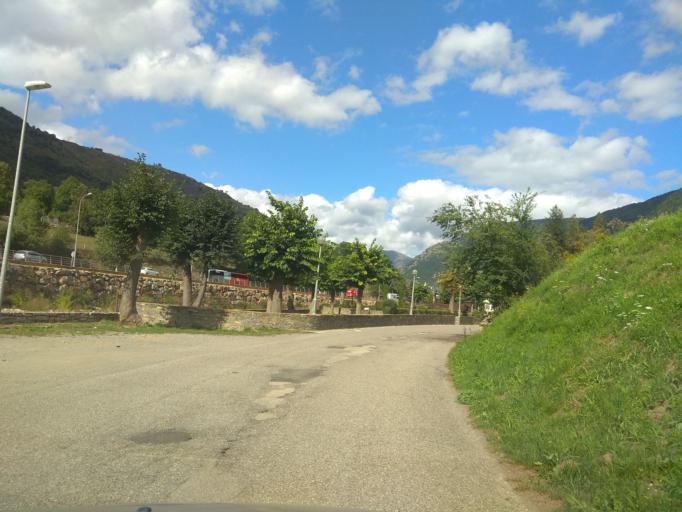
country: ES
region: Catalonia
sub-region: Provincia de Lleida
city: Les
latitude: 42.8077
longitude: 0.7072
